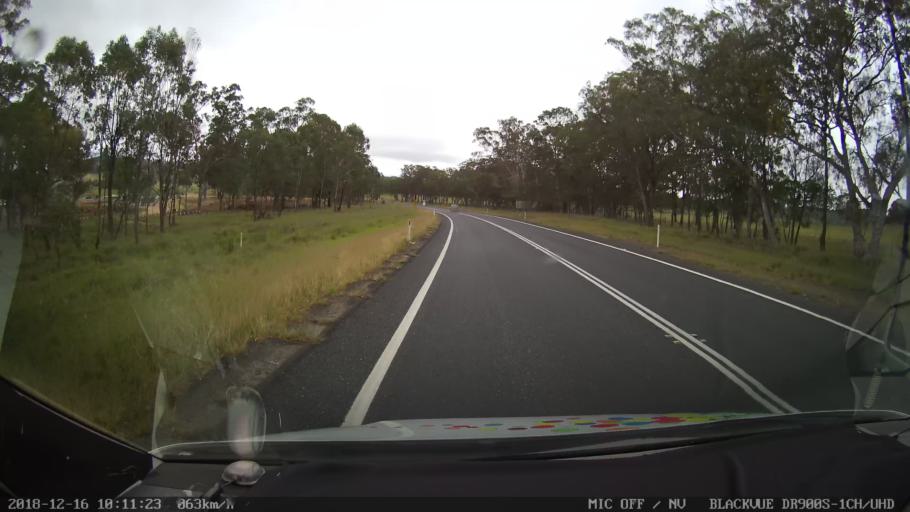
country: AU
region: New South Wales
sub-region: Glen Innes Severn
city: Glen Innes
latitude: -29.3135
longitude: 151.9322
